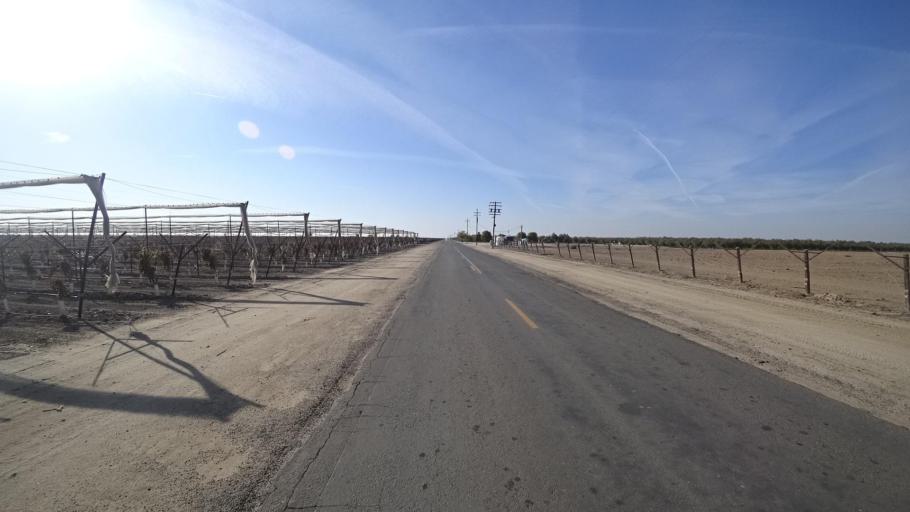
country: US
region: California
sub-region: Kern County
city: McFarland
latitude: 35.7032
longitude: -119.2663
